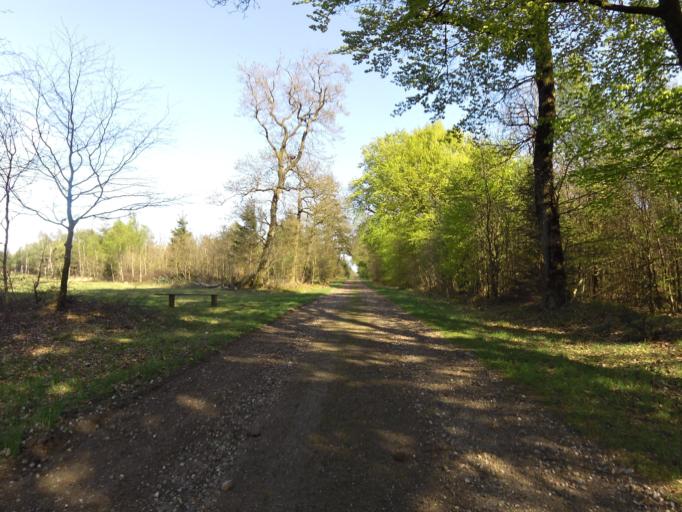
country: DK
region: South Denmark
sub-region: Tonder Kommune
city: Toftlund
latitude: 55.1940
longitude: 8.9500
